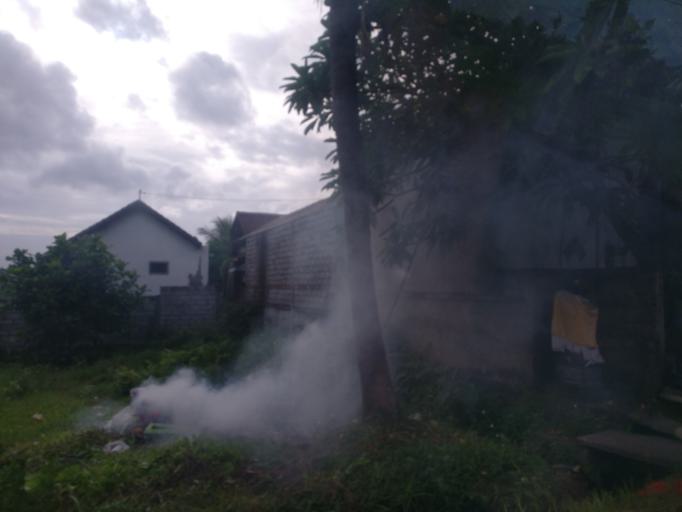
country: ID
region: Bali
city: Banjar Pasekan
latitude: -8.6061
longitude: 115.3146
